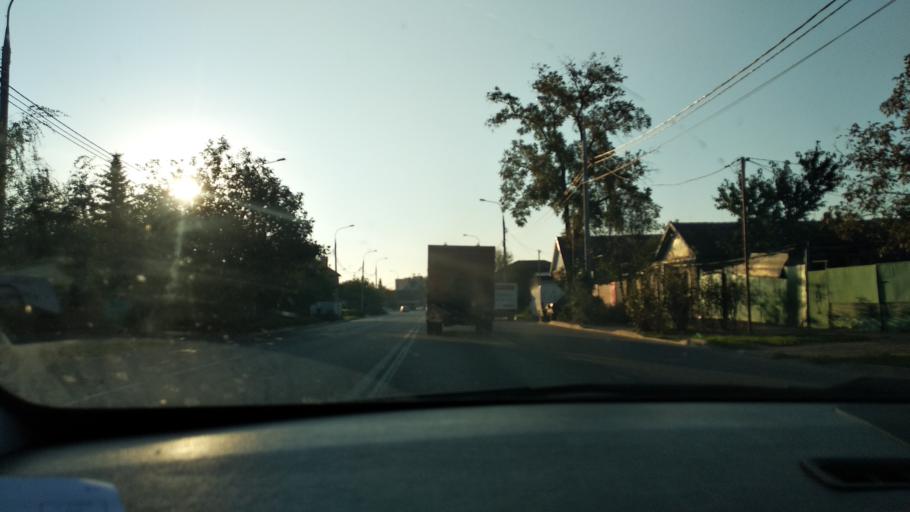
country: RU
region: Krasnodarskiy
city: Krasnodar
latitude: 45.0123
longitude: 39.0081
